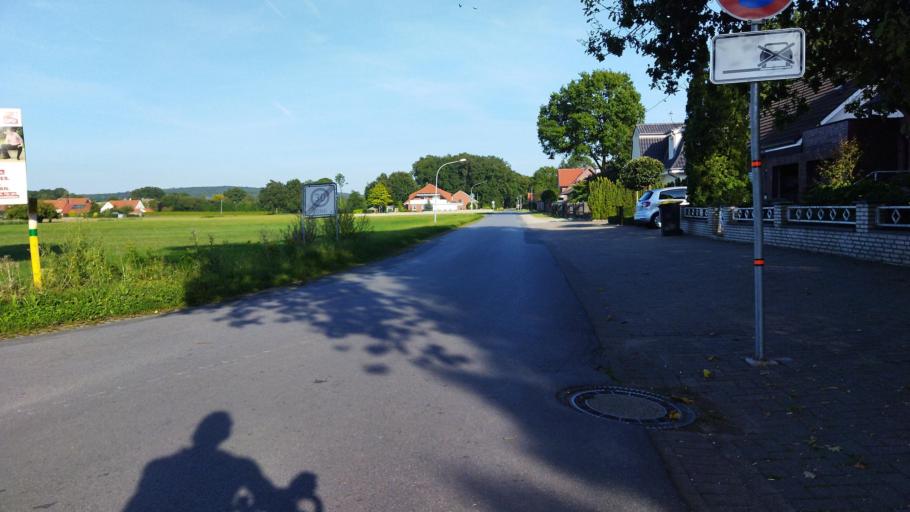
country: DE
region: Lower Saxony
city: Bad Laer
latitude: 52.0994
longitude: 8.0619
